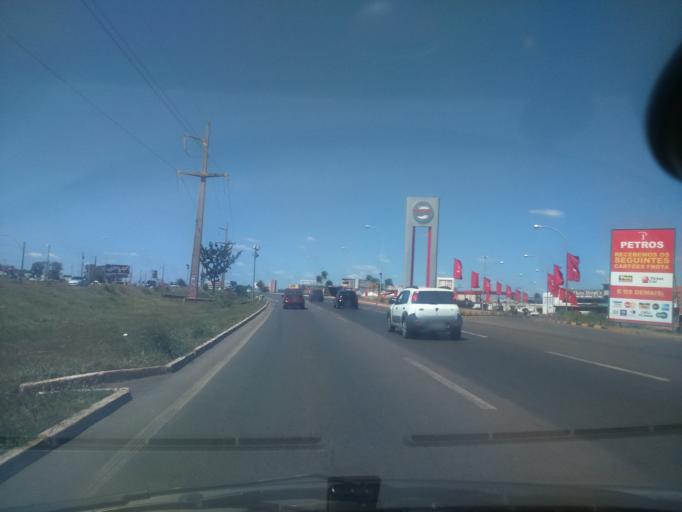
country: BR
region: Goias
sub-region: Luziania
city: Luziania
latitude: -16.0487
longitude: -48.0370
